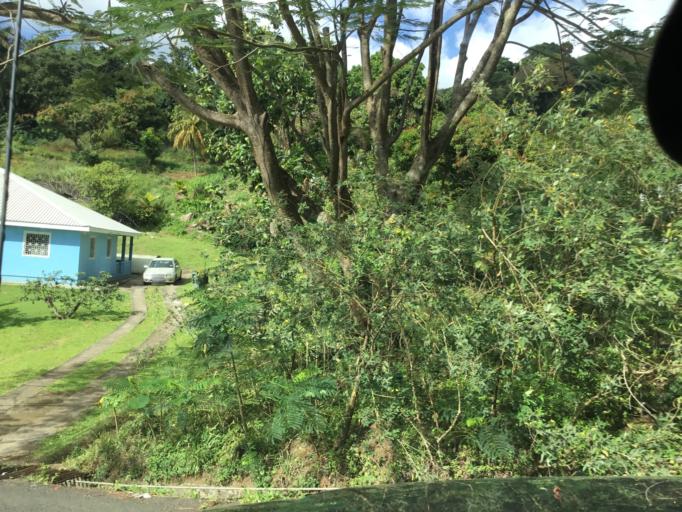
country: VC
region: Saint George
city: Kingstown
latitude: 13.1635
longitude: -61.2170
